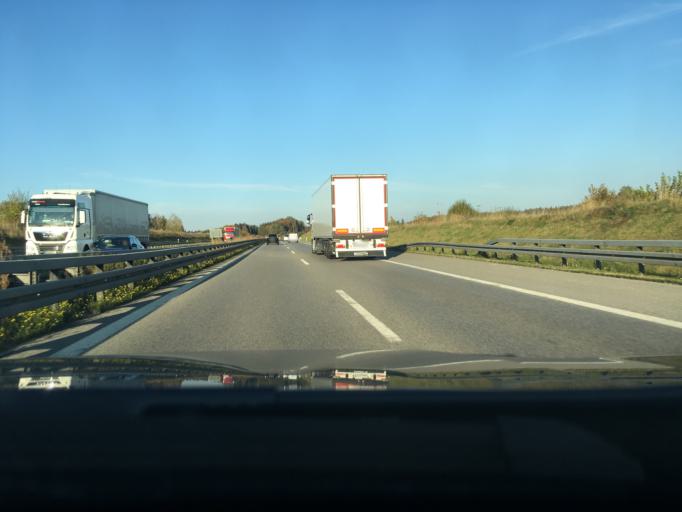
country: DE
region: Baden-Wuerttemberg
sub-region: Tuebingen Region
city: Kisslegg
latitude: 47.7675
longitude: 9.9244
